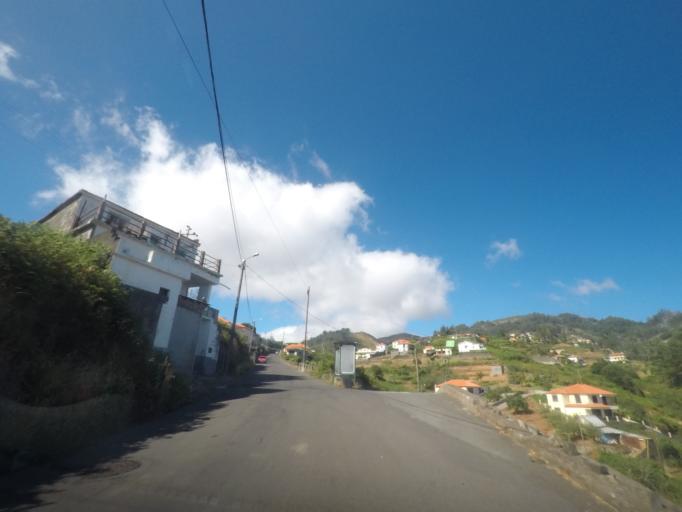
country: PT
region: Madeira
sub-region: Ribeira Brava
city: Campanario
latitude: 32.6955
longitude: -17.0267
